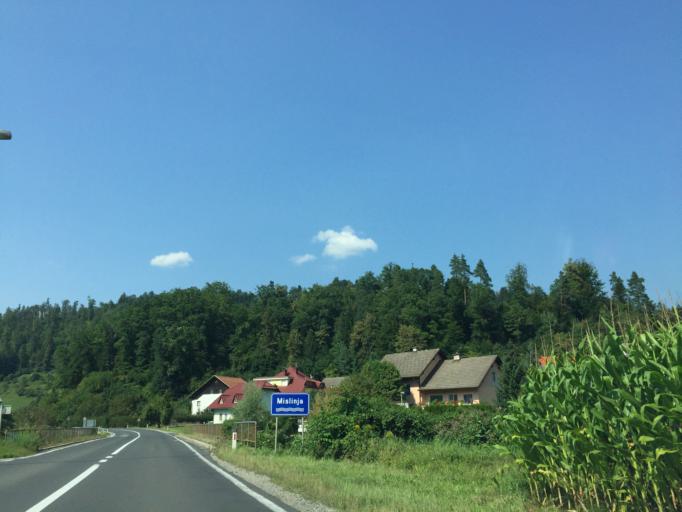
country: SI
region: Dravograd
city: Dravograd
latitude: 46.5665
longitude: 15.0387
